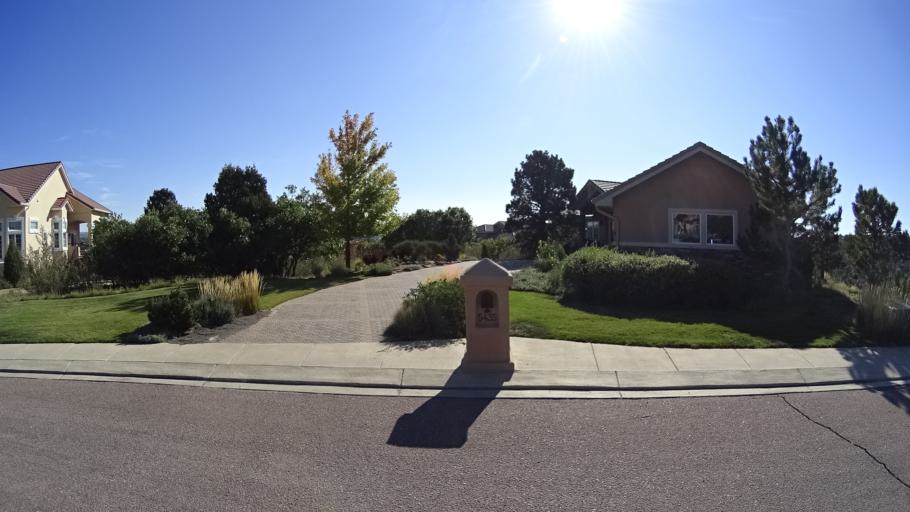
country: US
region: Colorado
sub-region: El Paso County
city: Colorado Springs
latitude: 38.9098
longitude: -104.8005
